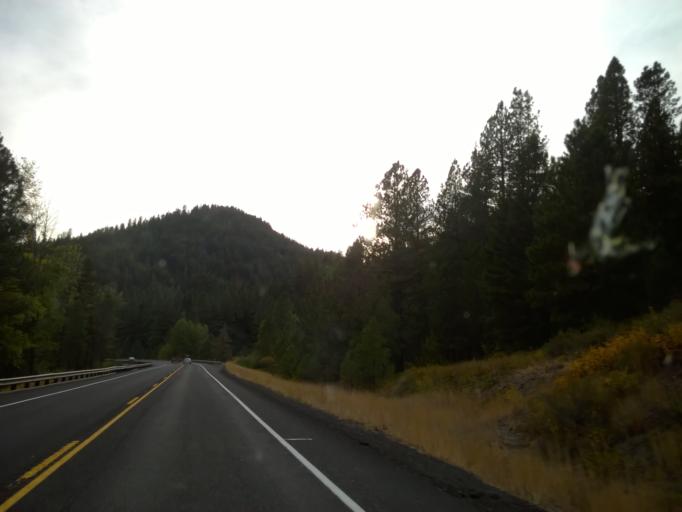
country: US
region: Washington
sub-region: Chelan County
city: Leavenworth
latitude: 47.3200
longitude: -120.6893
